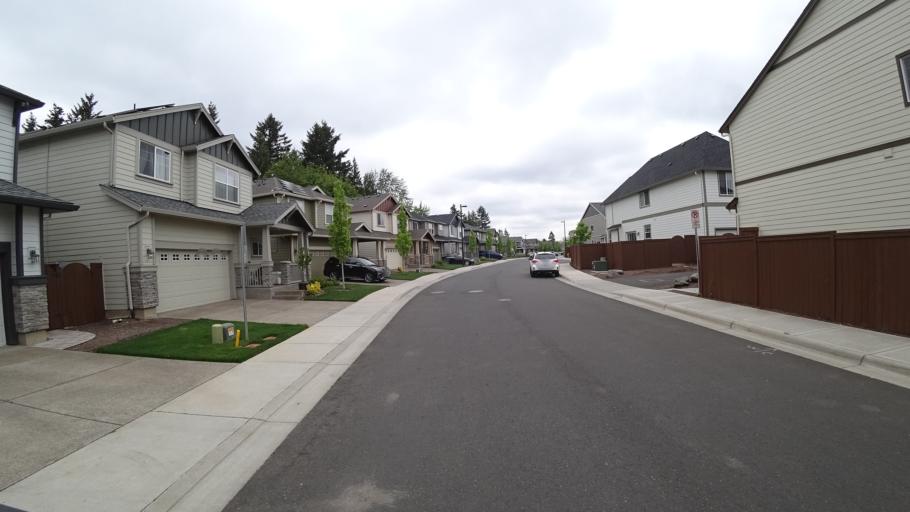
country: US
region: Oregon
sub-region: Washington County
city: Aloha
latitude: 45.5176
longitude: -122.8849
